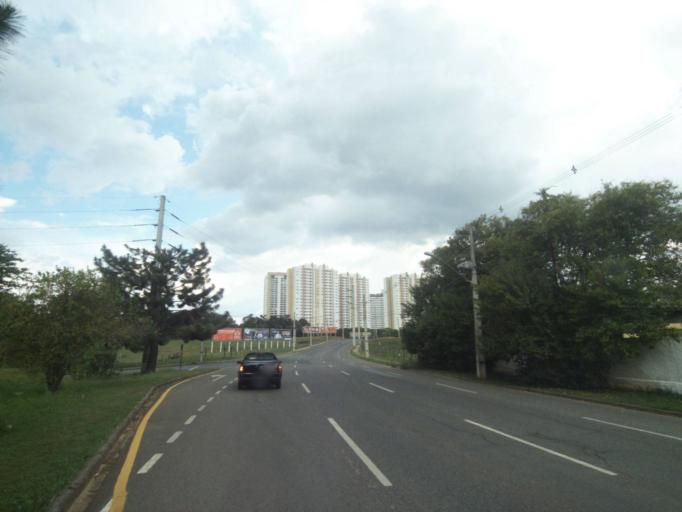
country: BR
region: Parana
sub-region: Curitiba
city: Curitiba
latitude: -25.4440
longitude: -49.3518
